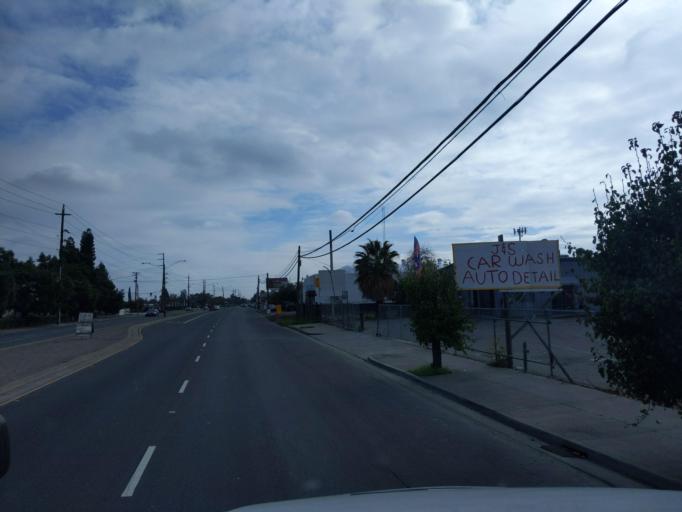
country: US
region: California
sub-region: San Joaquin County
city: August
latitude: 37.9795
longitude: -121.2821
